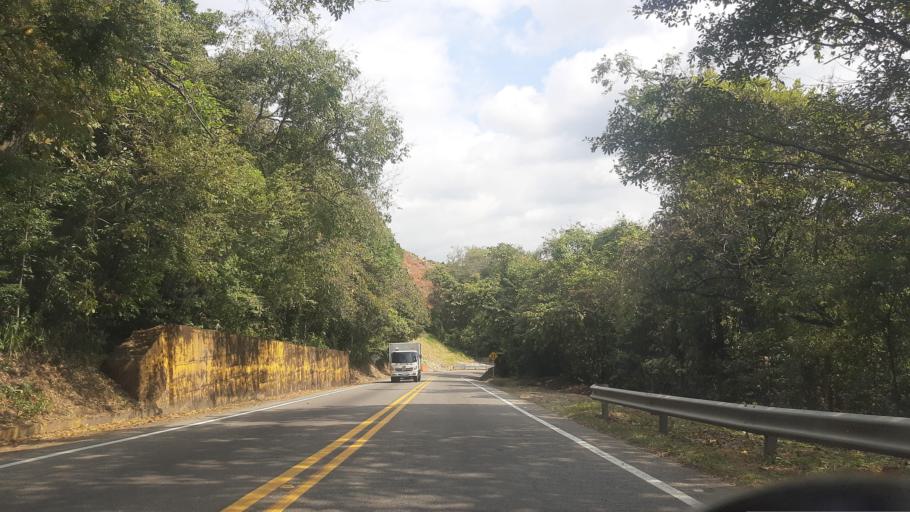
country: CO
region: Casanare
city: Monterrey
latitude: 4.8459
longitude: -72.8472
